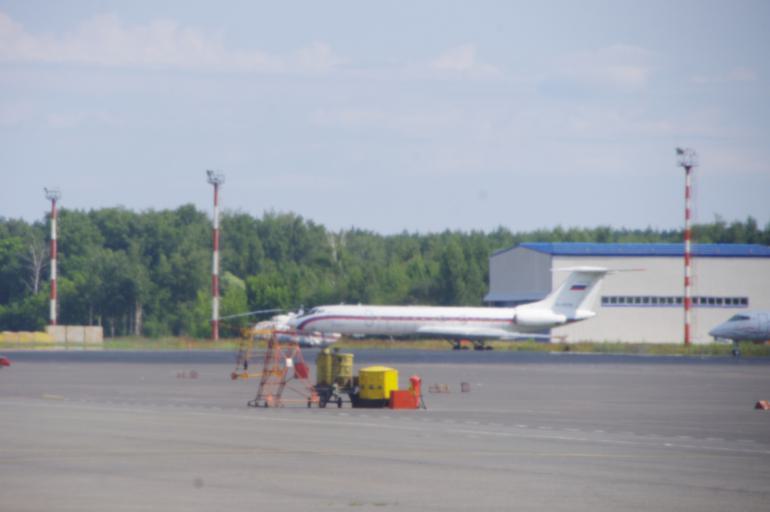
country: RU
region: Nizjnij Novgorod
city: Gorbatovka
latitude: 56.2191
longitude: 43.7857
